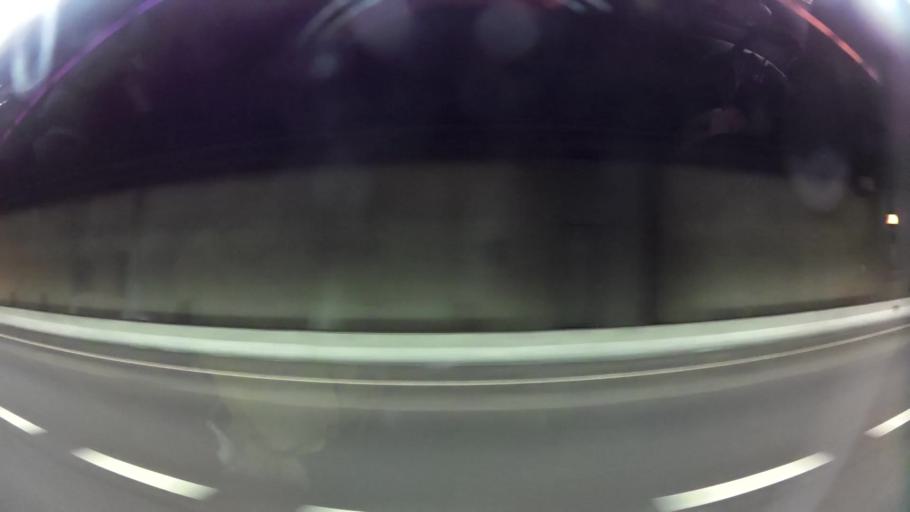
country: SG
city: Singapore
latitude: 1.3092
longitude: 103.8435
